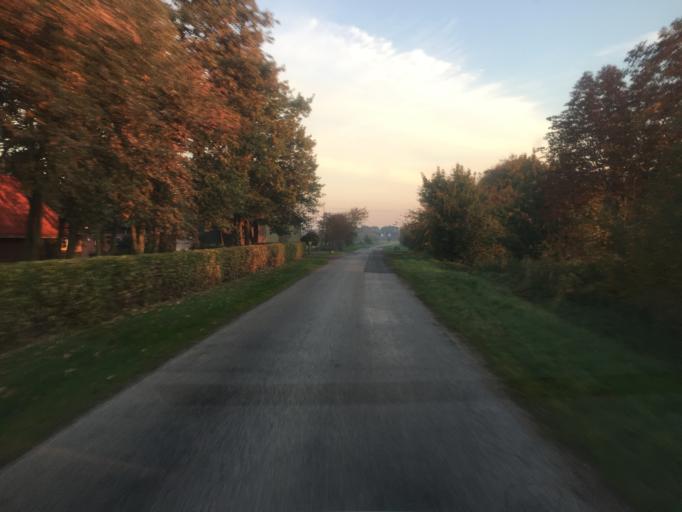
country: DK
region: South Denmark
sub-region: Tonder Kommune
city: Logumkloster
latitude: 55.0493
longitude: 9.0244
